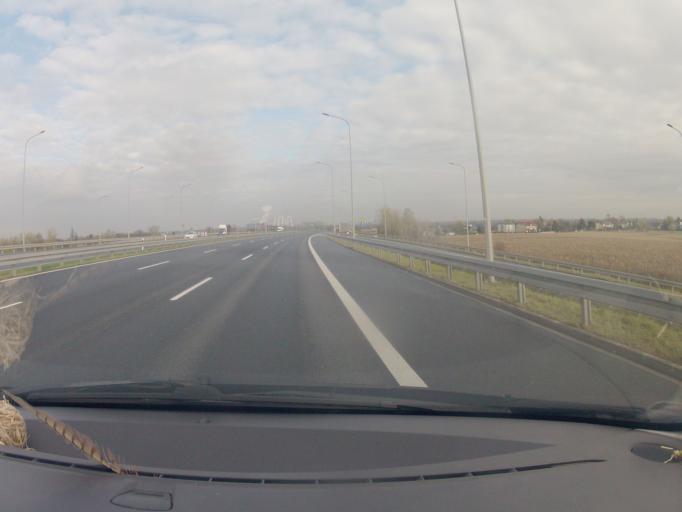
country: PL
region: Lesser Poland Voivodeship
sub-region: Powiat wielicki
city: Kokotow
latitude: 50.0389
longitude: 20.0651
